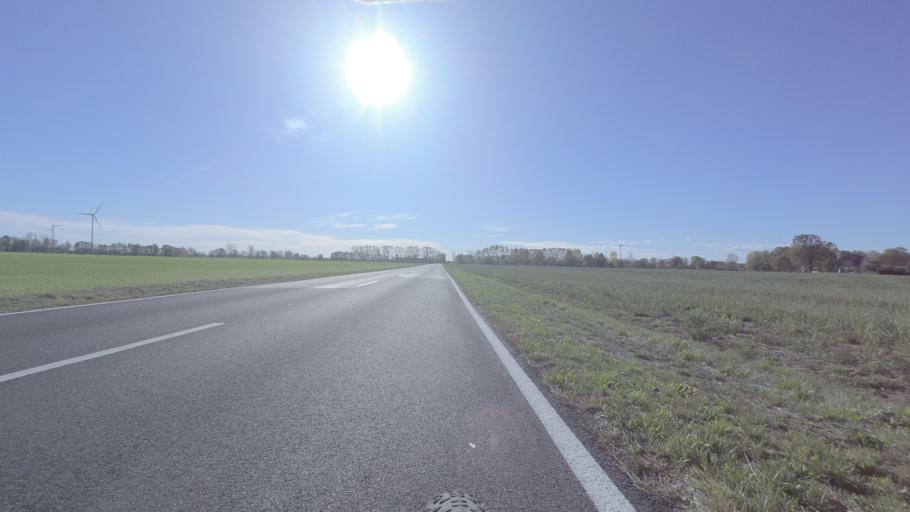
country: DE
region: Brandenburg
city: Elsterwerda
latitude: 51.4573
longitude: 13.4614
